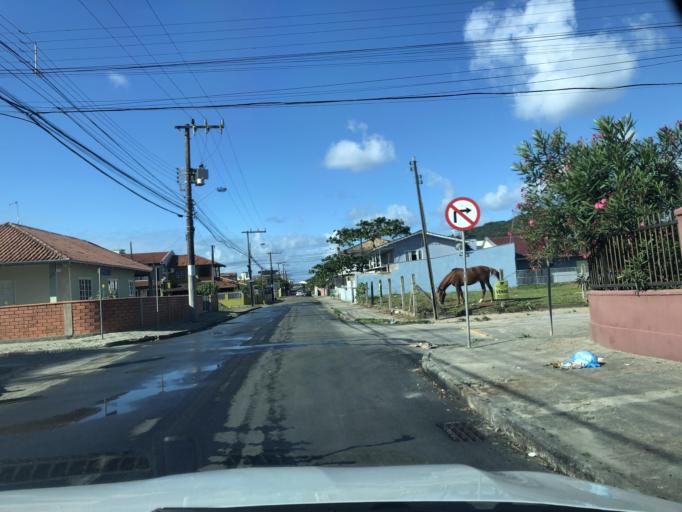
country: BR
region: Santa Catarina
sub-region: Sao Francisco Do Sul
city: Sao Francisco do Sul
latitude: -26.2324
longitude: -48.5054
